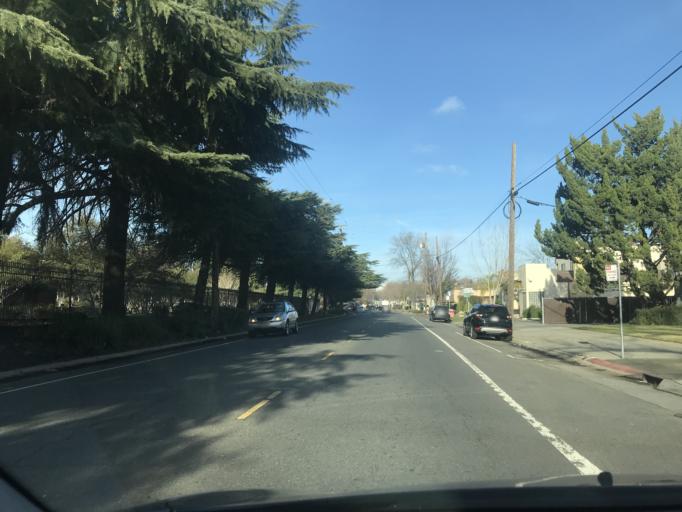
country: US
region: California
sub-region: Sacramento County
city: Sacramento
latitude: 38.5603
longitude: -121.4999
